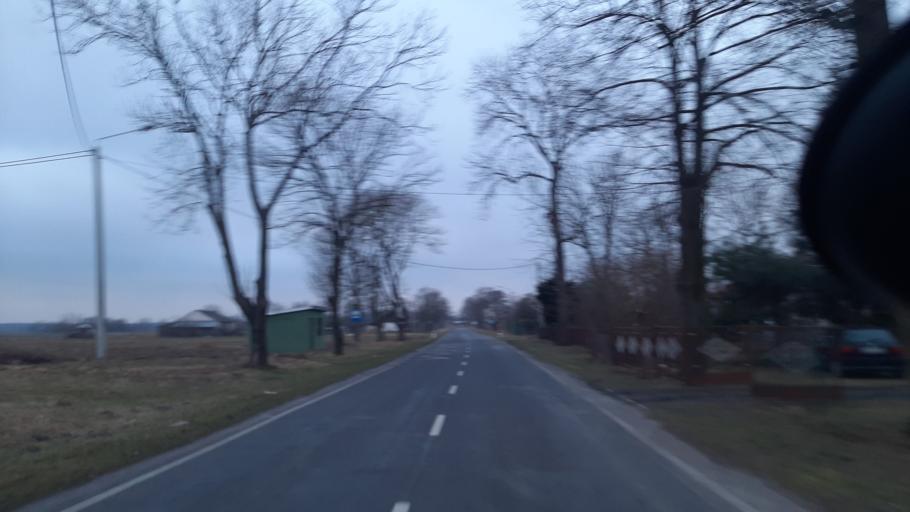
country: PL
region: Lublin Voivodeship
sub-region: Powiat parczewski
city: Debowa Kloda
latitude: 51.6364
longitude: 23.0599
